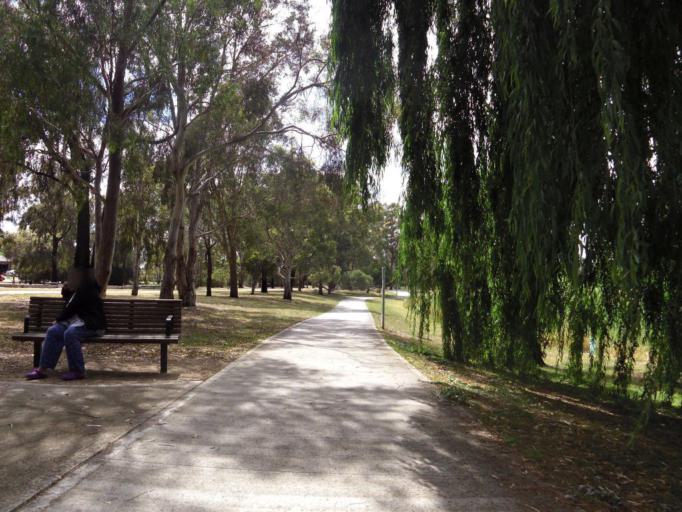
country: AU
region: Victoria
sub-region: Banyule
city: Bundoora
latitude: -37.6946
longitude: 145.0505
